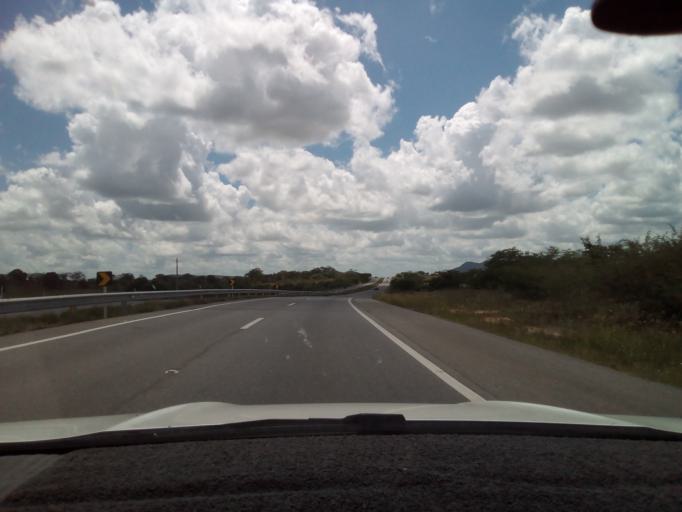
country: BR
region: Paraiba
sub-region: Gurinhem
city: Gurinhem
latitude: -7.1939
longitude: -35.4818
